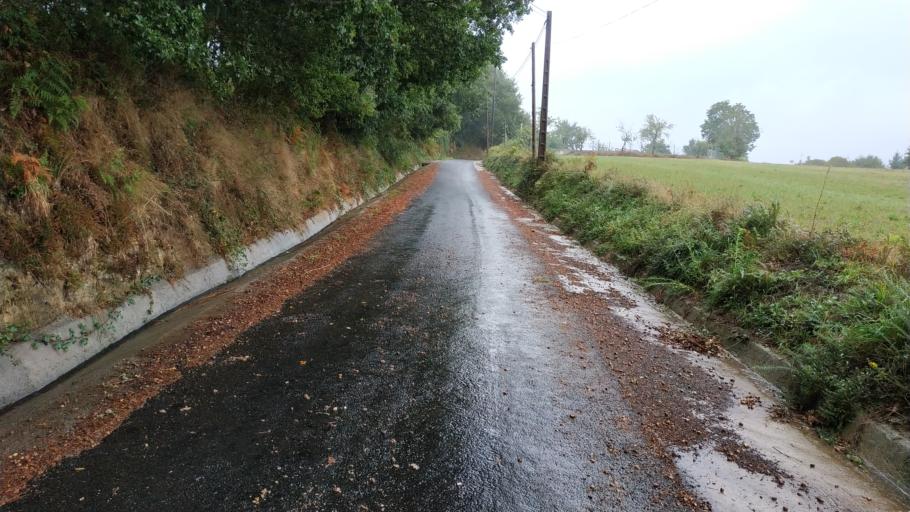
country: ES
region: Galicia
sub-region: Provincia da Coruna
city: Negreira
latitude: 42.9079
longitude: -8.7427
